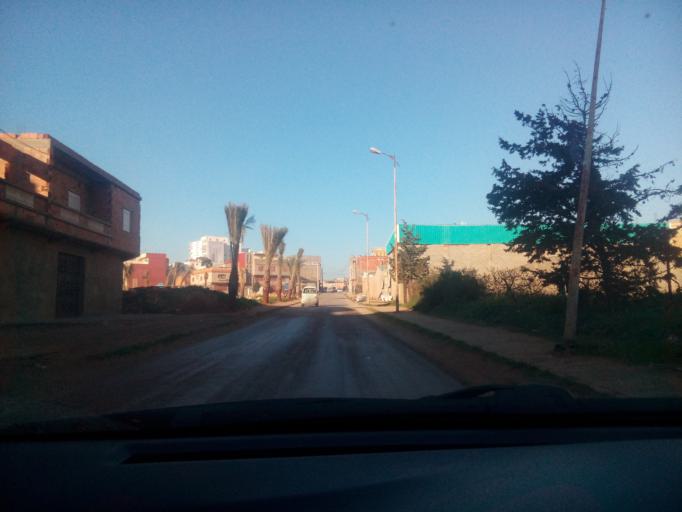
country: DZ
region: Oran
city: Bir el Djir
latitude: 35.7564
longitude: -0.5360
